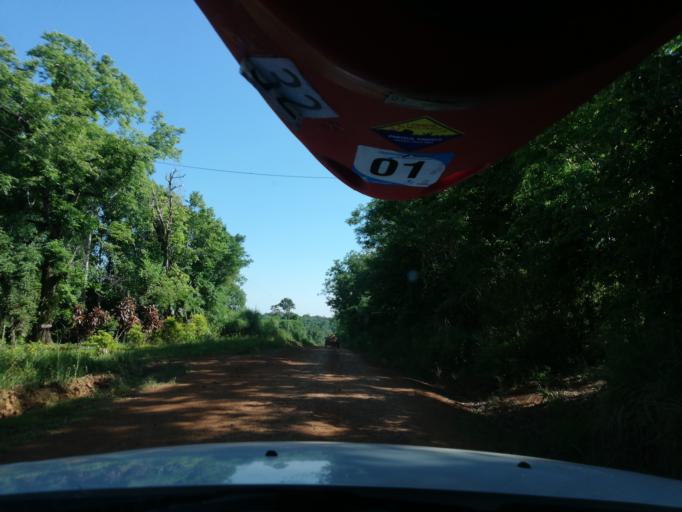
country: AR
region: Misiones
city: Puerto Leoni
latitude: -26.9752
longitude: -55.1647
